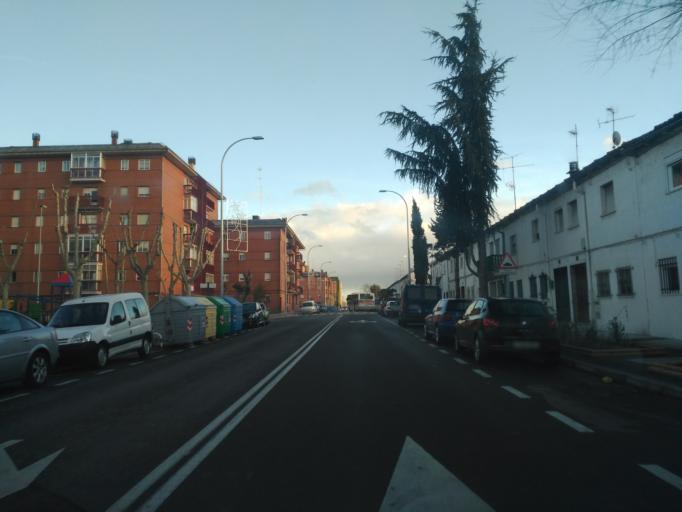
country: ES
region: Castille and Leon
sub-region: Provincia de Salamanca
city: Salamanca
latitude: 40.9520
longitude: -5.6667
